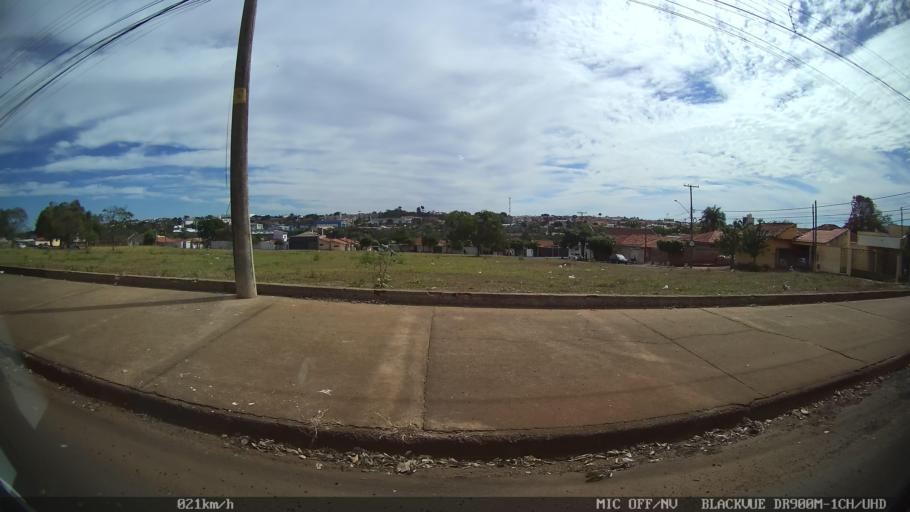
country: BR
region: Sao Paulo
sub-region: Catanduva
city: Catanduva
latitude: -21.1573
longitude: -48.9781
